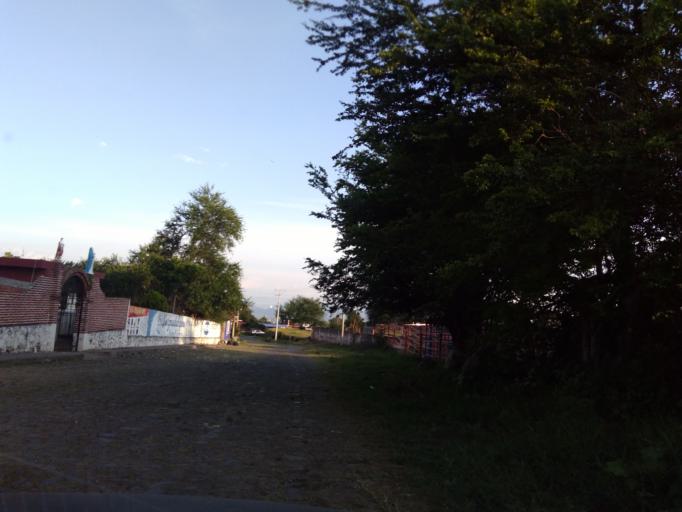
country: MX
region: Jalisco
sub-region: Tonila
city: San Marcos
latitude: 19.4481
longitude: -103.5100
